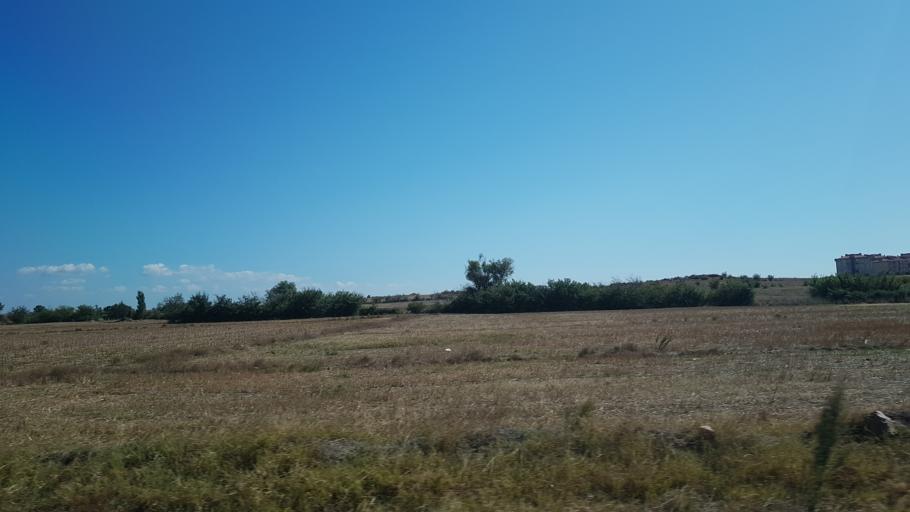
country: TR
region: Kirklareli
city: Kirklareli
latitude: 41.7634
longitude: 27.2224
